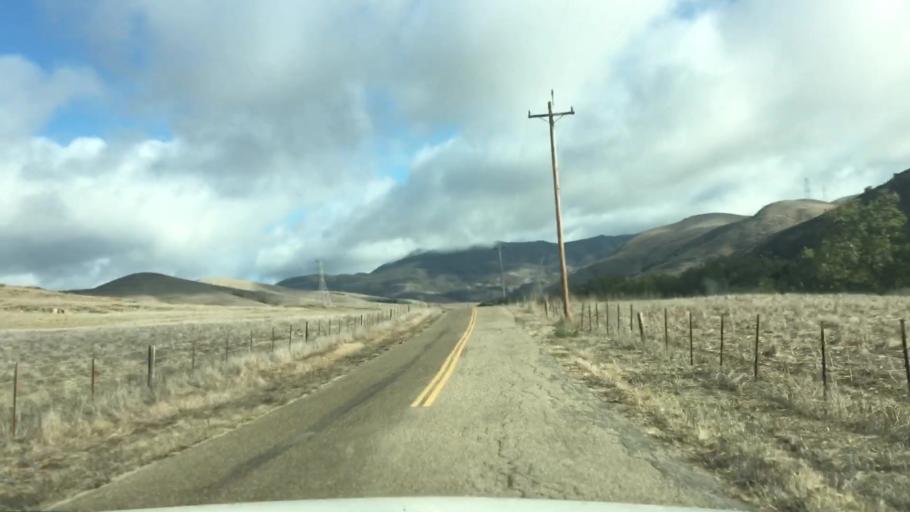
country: US
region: California
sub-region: San Luis Obispo County
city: Morro Bay
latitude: 35.3742
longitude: -120.7973
